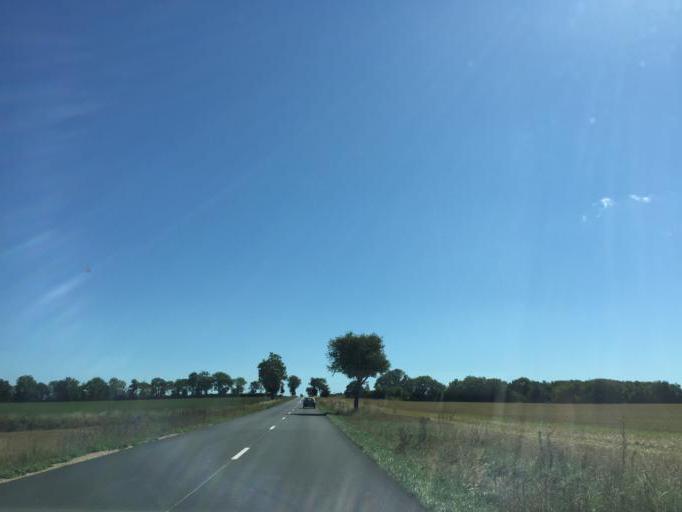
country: FR
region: Midi-Pyrenees
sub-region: Departement de l'Aveyron
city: La Cavalerie
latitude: 44.0157
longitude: 3.0846
